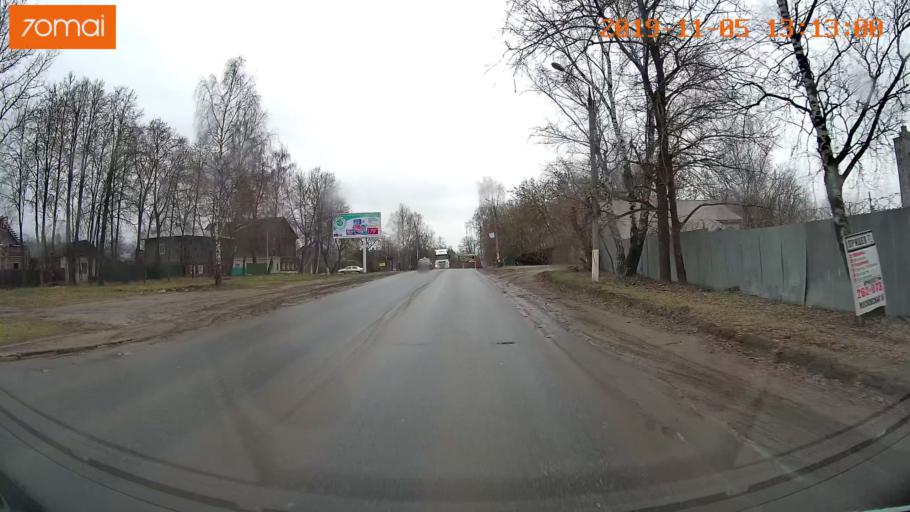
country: RU
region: Ivanovo
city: Shuya
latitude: 56.8540
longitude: 41.3532
